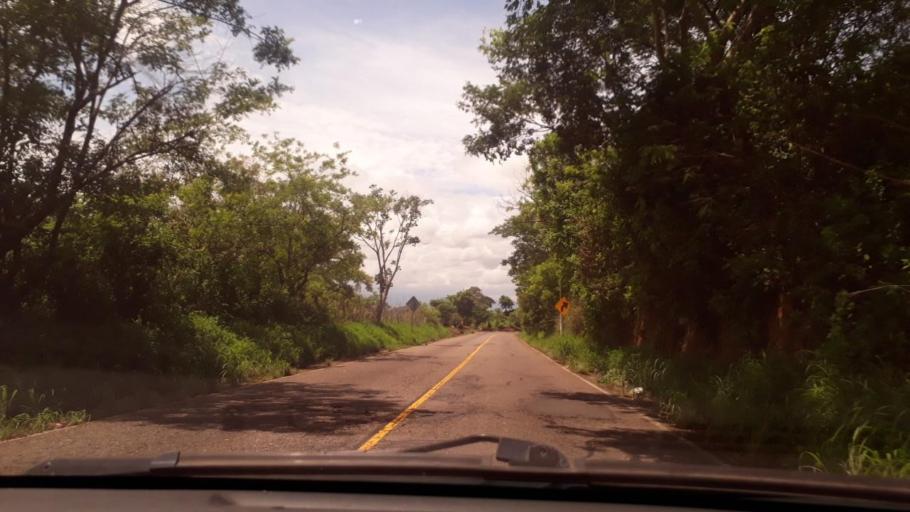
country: GT
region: Jutiapa
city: Jalpatagua
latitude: 14.1809
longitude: -90.0443
